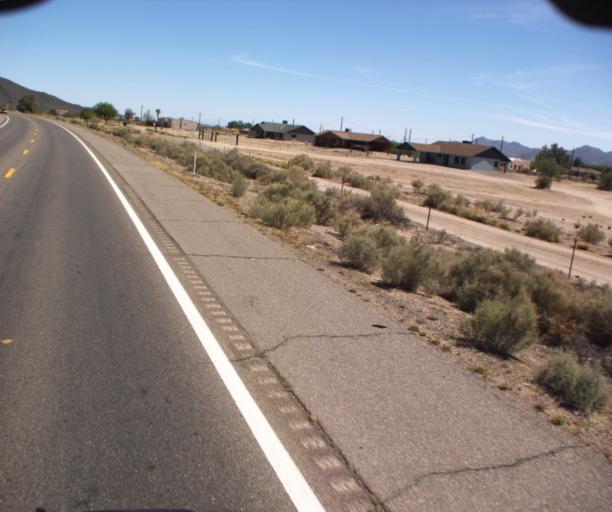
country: US
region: Arizona
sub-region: Pinal County
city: Sacaton
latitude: 33.1227
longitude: -111.7423
